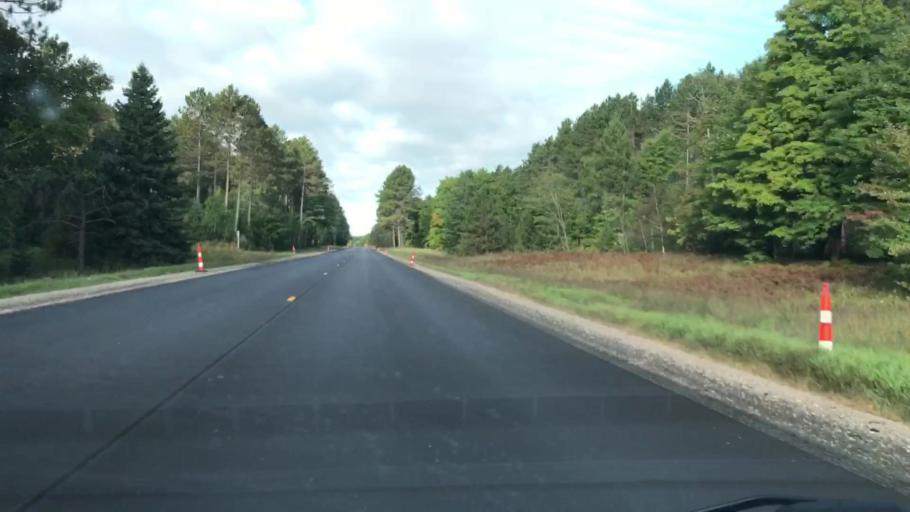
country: US
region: Michigan
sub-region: Luce County
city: Newberry
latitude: 46.3464
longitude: -85.0097
